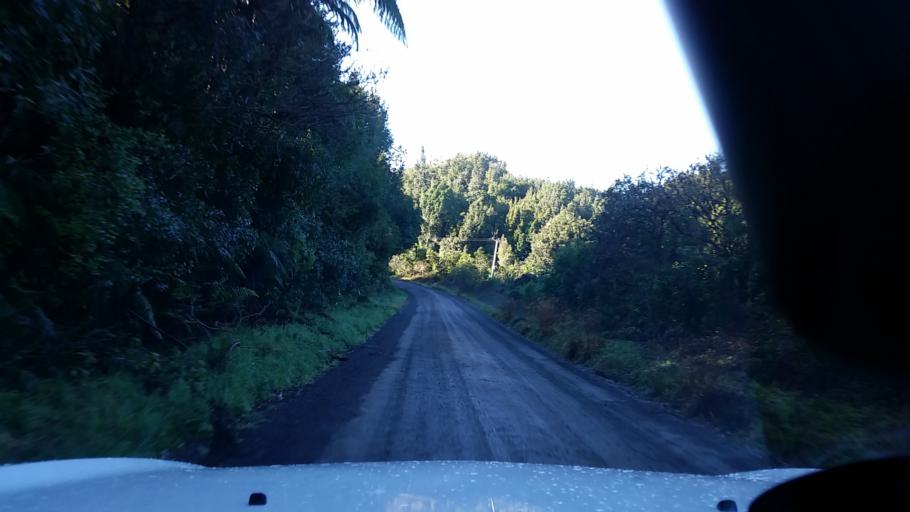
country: NZ
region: Bay of Plenty
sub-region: Kawerau District
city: Kawerau
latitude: -38.0179
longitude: 176.4740
